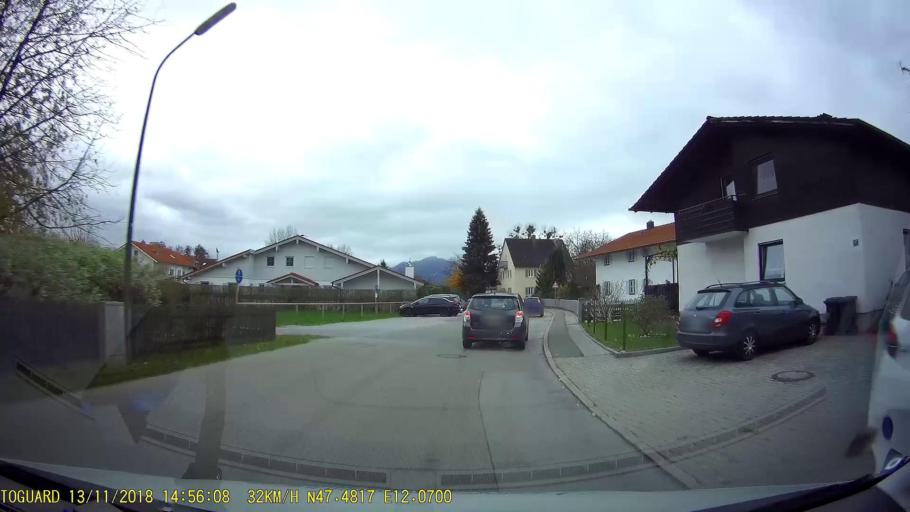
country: DE
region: Bavaria
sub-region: Upper Bavaria
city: Raubling
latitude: 47.8027
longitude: 12.1167
